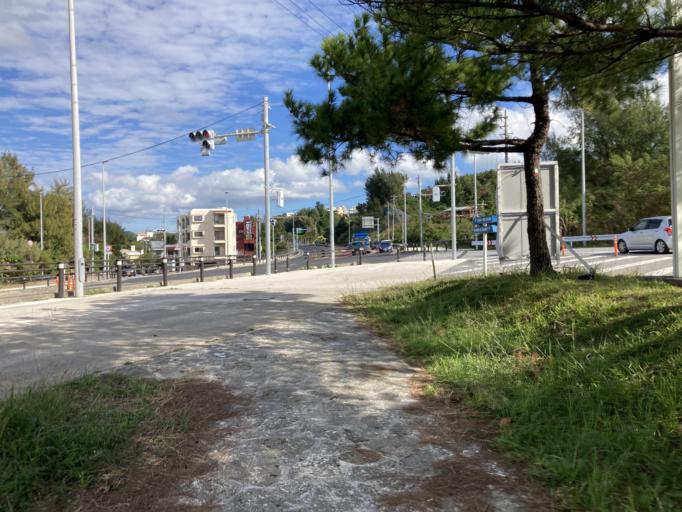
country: JP
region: Okinawa
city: Ishikawa
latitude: 26.4357
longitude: 127.7960
